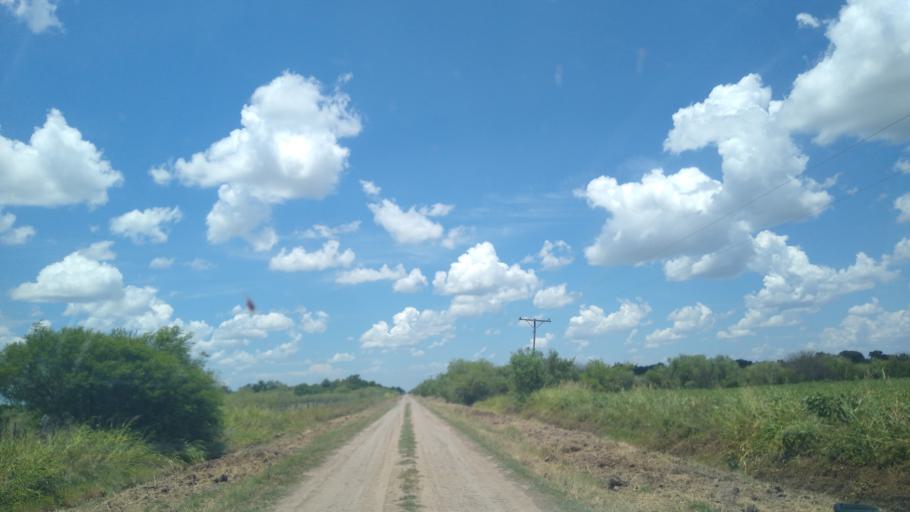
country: AR
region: Chaco
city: Presidencia Roque Saenz Pena
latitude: -26.7366
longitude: -60.3315
